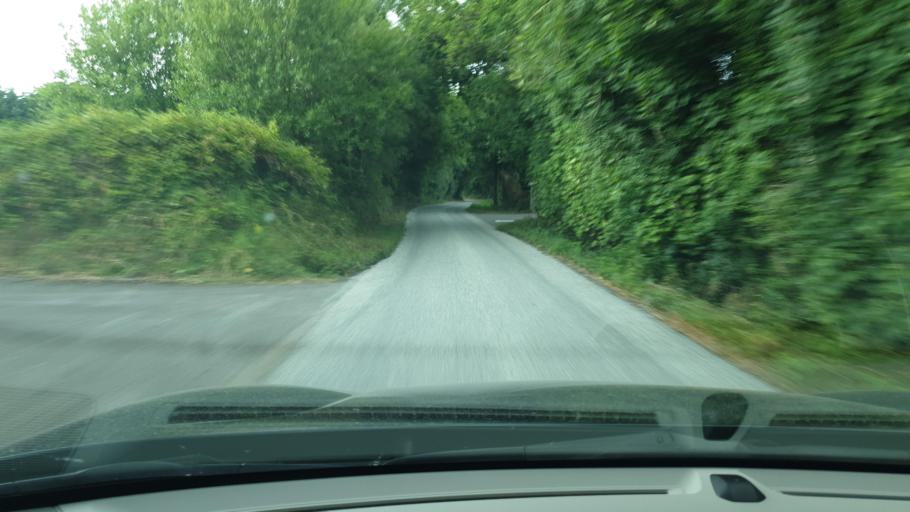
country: IE
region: Leinster
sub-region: An Mhi
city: Dunshaughlin
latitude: 53.4952
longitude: -6.5099
